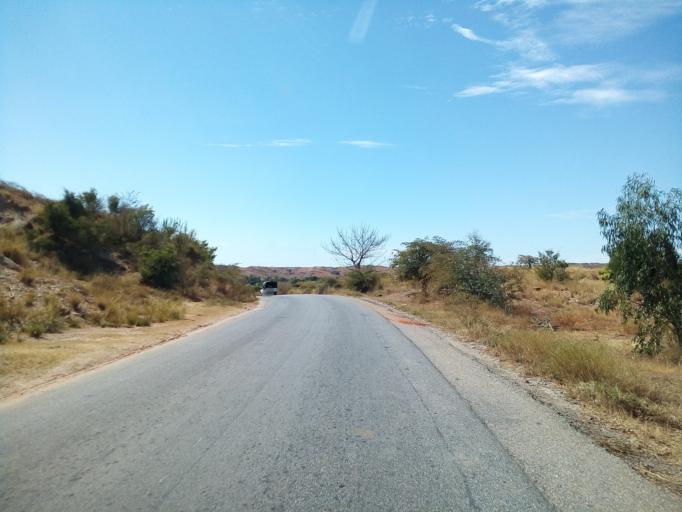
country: MG
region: Betsiboka
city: Maevatanana
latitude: -16.9184
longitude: 46.8686
